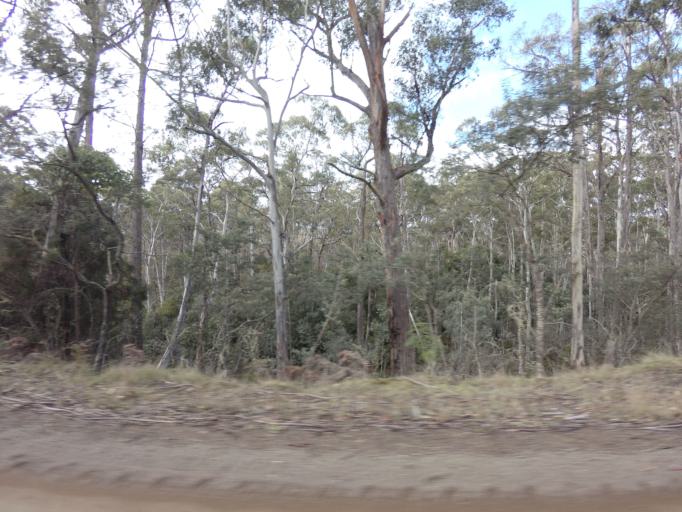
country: AU
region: Tasmania
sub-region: Derwent Valley
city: New Norfolk
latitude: -42.7518
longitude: 146.8756
